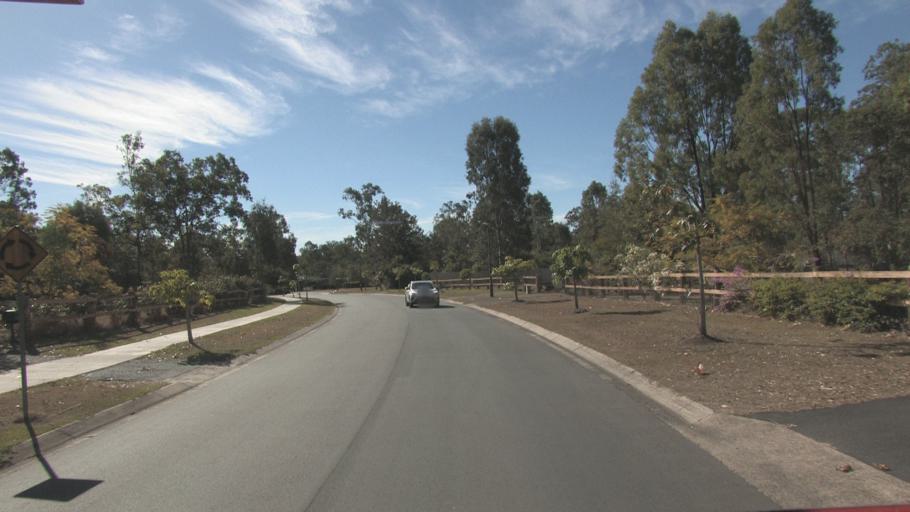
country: AU
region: Queensland
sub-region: Logan
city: North Maclean
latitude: -27.8100
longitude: 152.9628
